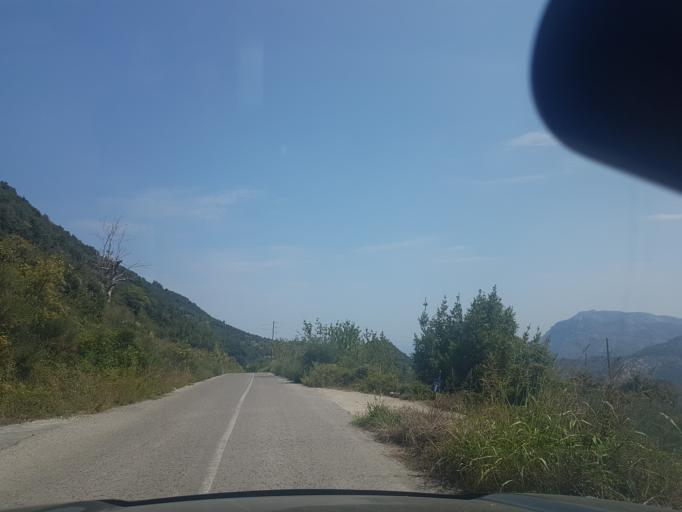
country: GR
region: Central Greece
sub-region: Nomos Evvoias
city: Kymi
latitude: 38.6472
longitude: 23.9003
